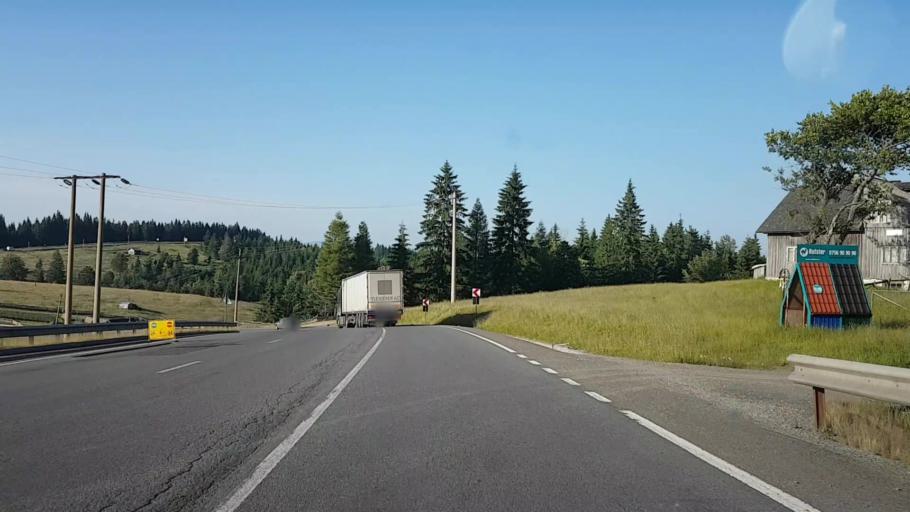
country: RO
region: Bistrita-Nasaud
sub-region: Comuna Lunca Ilvei
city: Lunca Ilvei
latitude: 47.2734
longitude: 25.0278
